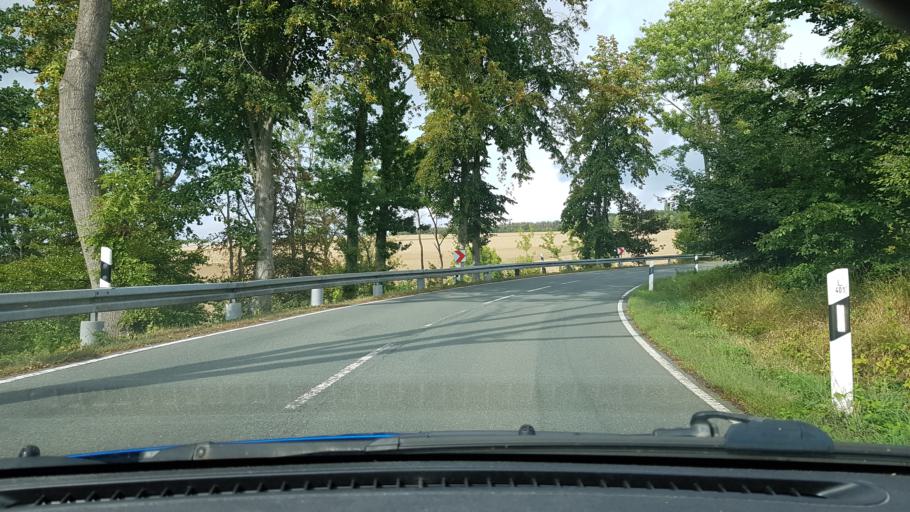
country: DE
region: Lower Saxony
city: Messenkamp
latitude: 52.2405
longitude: 9.4276
